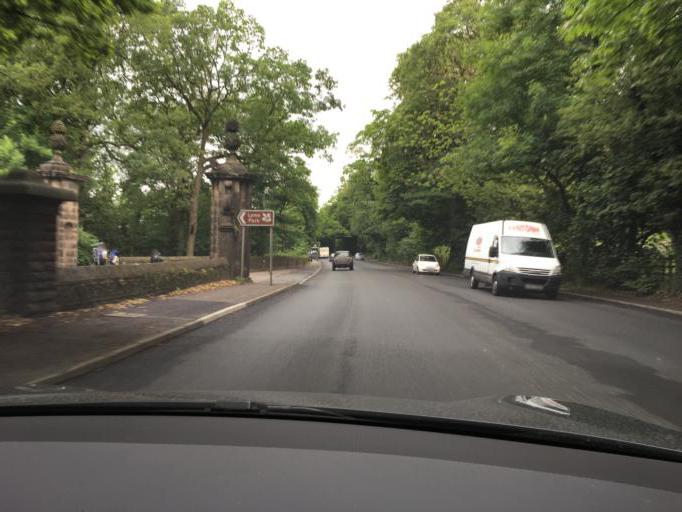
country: GB
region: England
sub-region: Cheshire East
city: Disley
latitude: 53.3570
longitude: -2.0532
